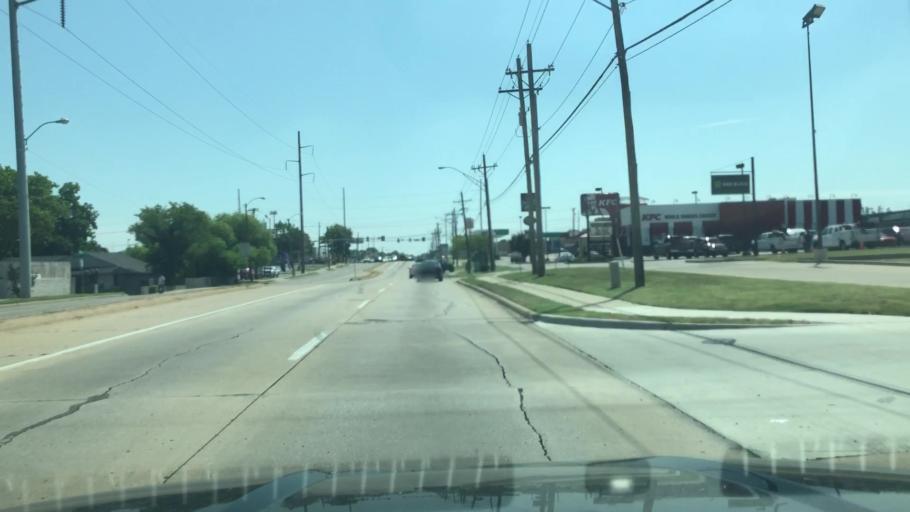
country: US
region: Oklahoma
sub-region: Tulsa County
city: Broken Arrow
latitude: 36.1334
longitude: -95.8538
